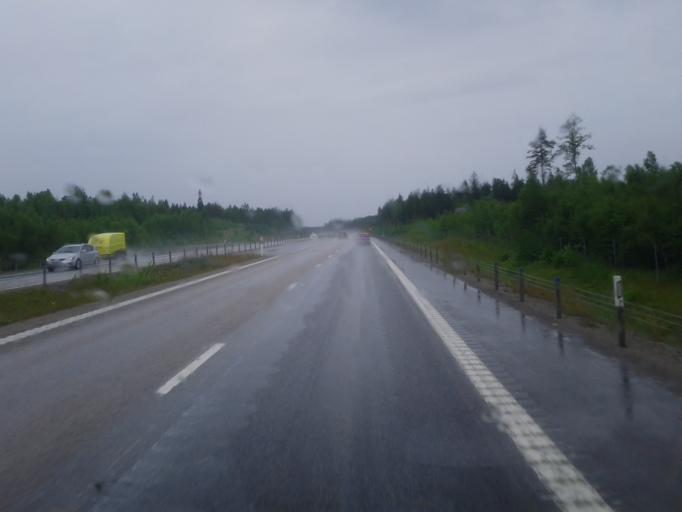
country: SE
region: Uppsala
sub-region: Tierps Kommun
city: Tierp
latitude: 60.2242
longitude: 17.4989
